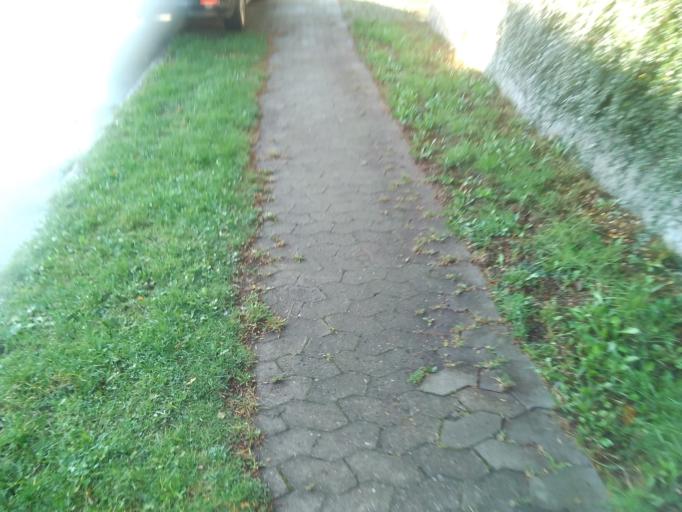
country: DK
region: Capital Region
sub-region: Gladsaxe Municipality
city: Buddinge
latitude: 55.7208
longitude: 12.5037
